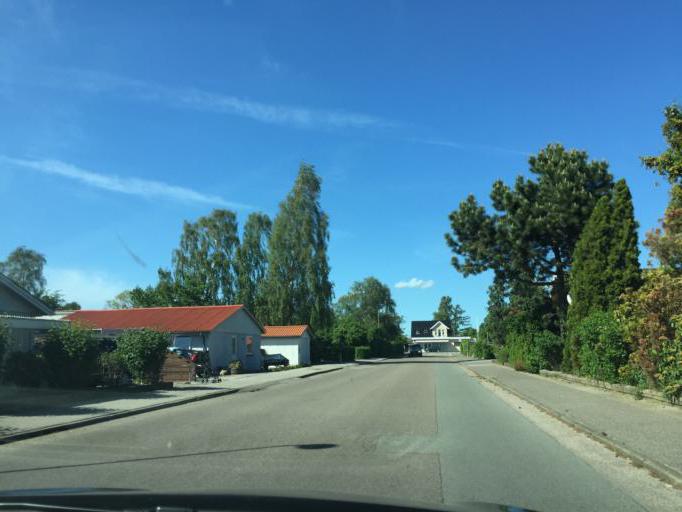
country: DK
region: Zealand
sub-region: Stevns Kommune
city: Harlev
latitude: 55.3510
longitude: 12.2325
